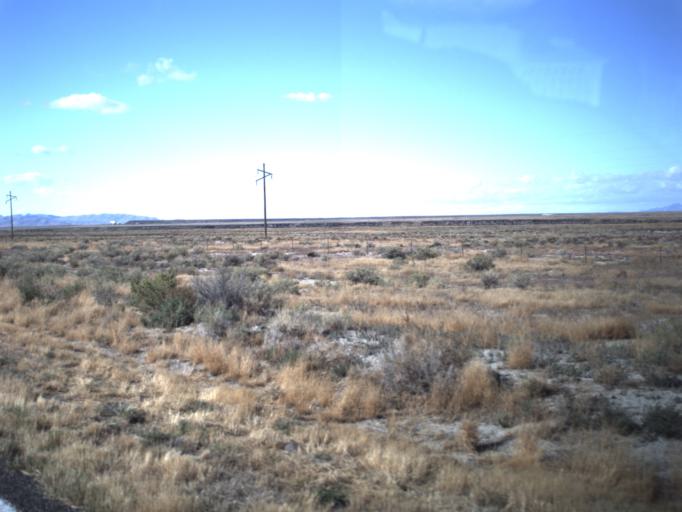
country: US
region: Utah
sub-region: Millard County
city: Delta
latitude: 39.2074
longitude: -112.6835
